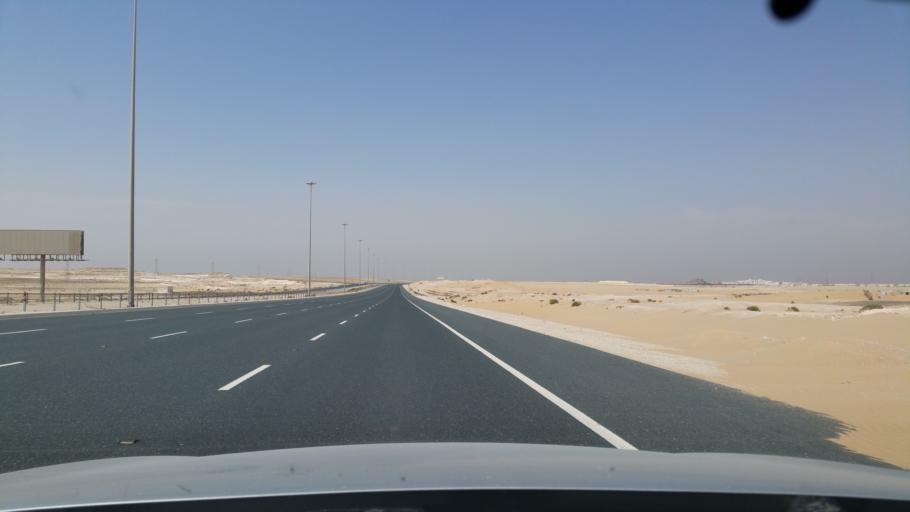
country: QA
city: Umm Bab
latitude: 24.8592
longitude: 50.8991
